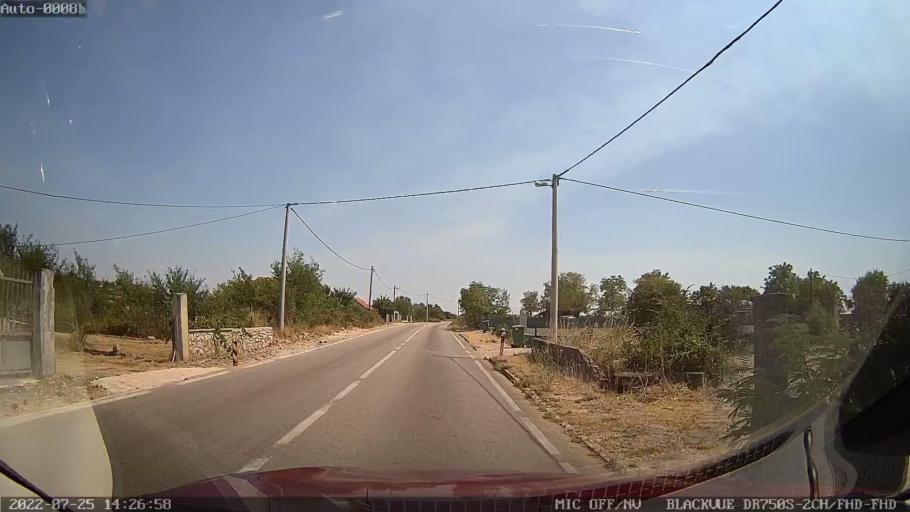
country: HR
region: Zadarska
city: Policnik
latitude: 44.1360
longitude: 15.3419
